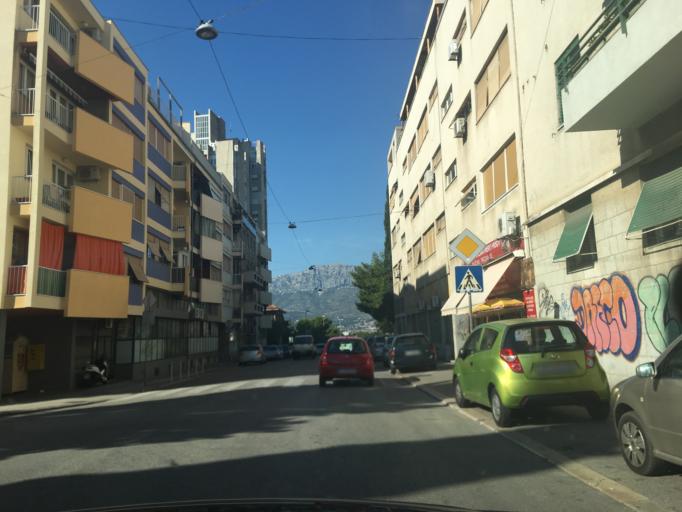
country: HR
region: Splitsko-Dalmatinska
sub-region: Grad Split
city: Split
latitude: 43.5166
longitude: 16.4351
